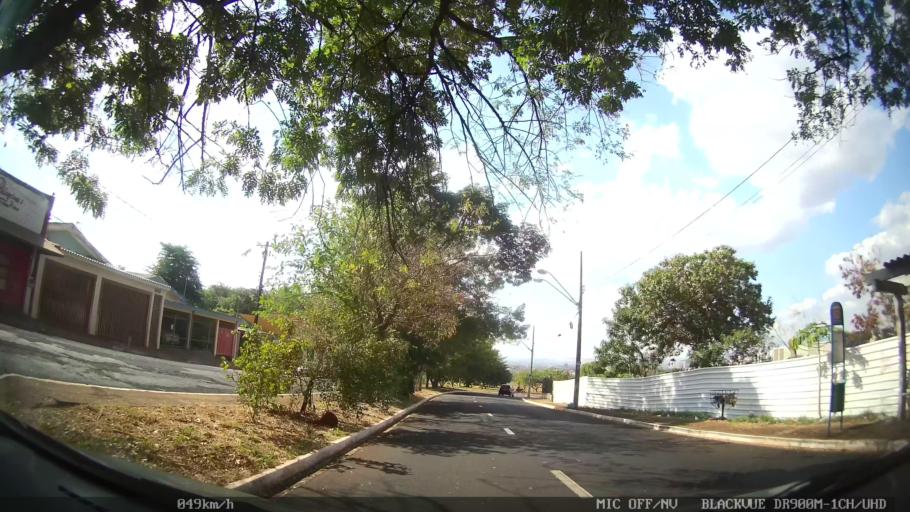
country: BR
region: Sao Paulo
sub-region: Ribeirao Preto
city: Ribeirao Preto
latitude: -21.1882
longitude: -47.8357
